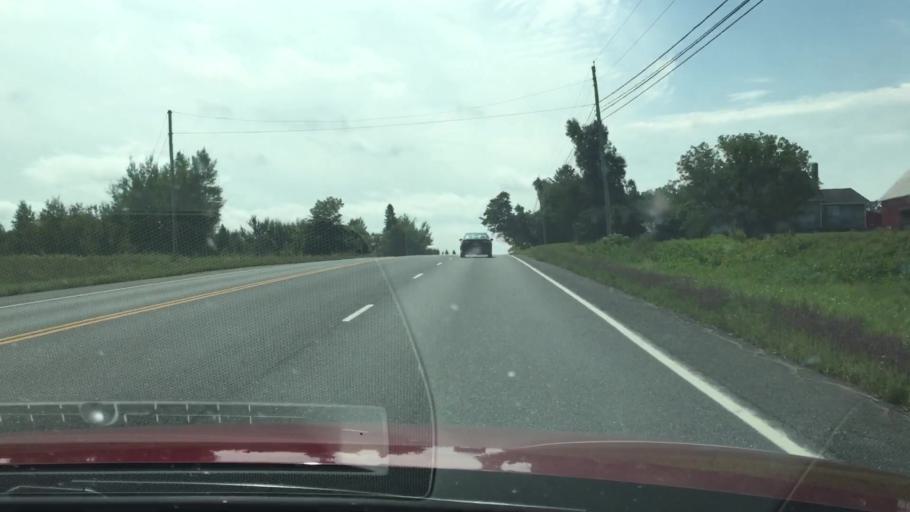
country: CA
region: New Brunswick
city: Florenceville-Bristol
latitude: 46.3968
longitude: -67.8430
